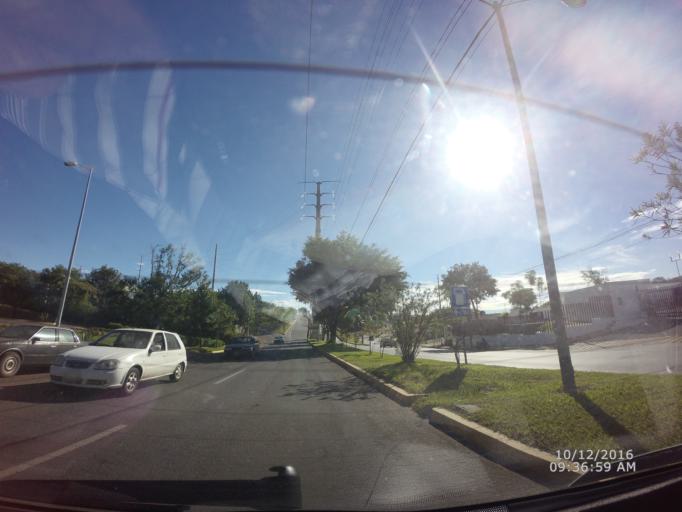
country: TR
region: Sivas
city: Karayun
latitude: 39.6693
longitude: 37.2954
